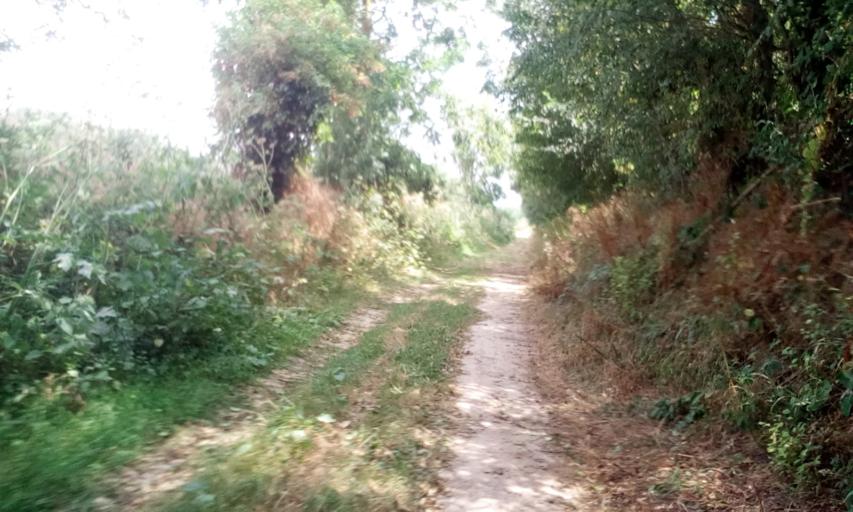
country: FR
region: Lower Normandy
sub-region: Departement du Calvados
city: Douvres-la-Delivrande
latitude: 49.2935
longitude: -0.3963
